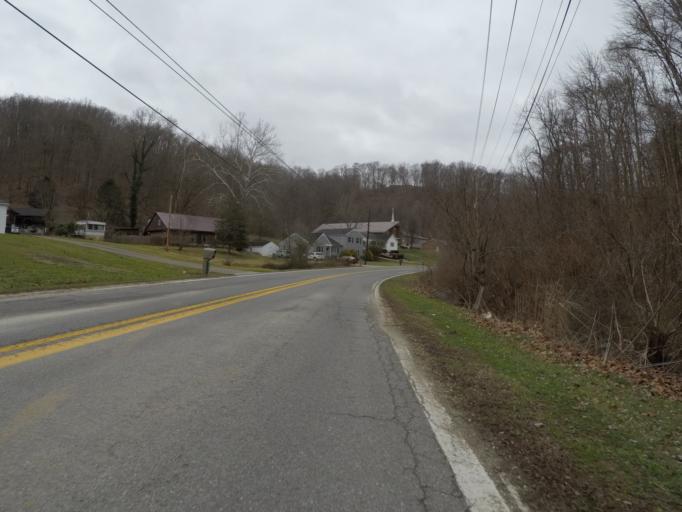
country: US
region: West Virginia
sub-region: Cabell County
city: Barboursville
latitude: 38.4542
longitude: -82.2977
